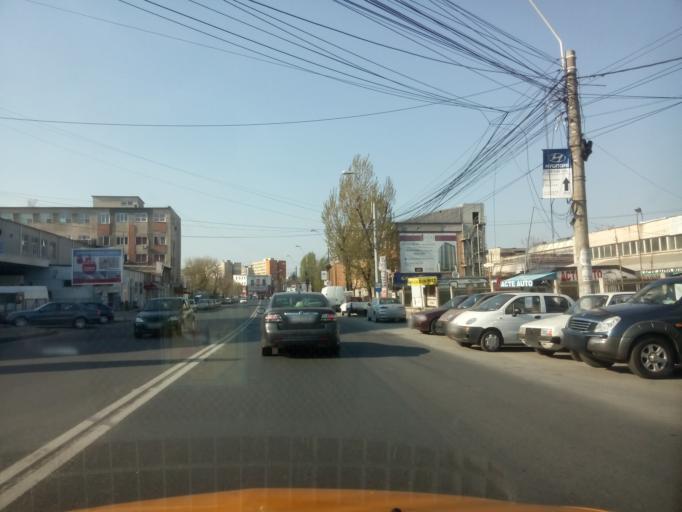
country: RO
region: Ilfov
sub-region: Comuna Popesti-Leordeni
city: Popesti-Leordeni
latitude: 44.4042
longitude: 26.1425
